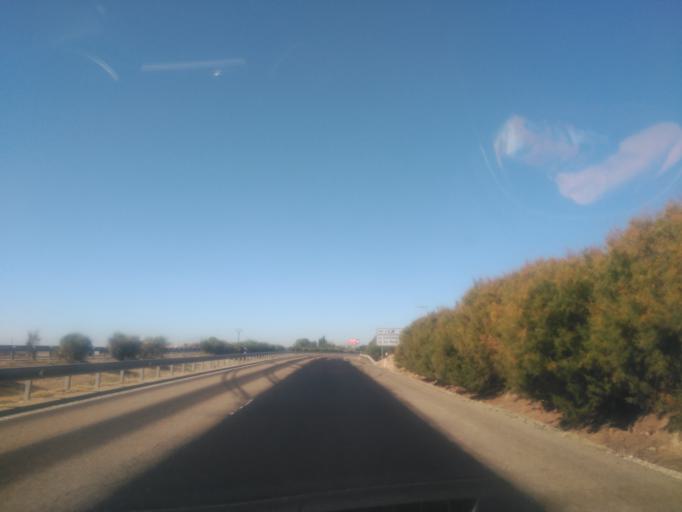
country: ES
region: Castille and Leon
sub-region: Provincia de Valladolid
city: Cisterniga
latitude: 41.5973
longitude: -4.6470
